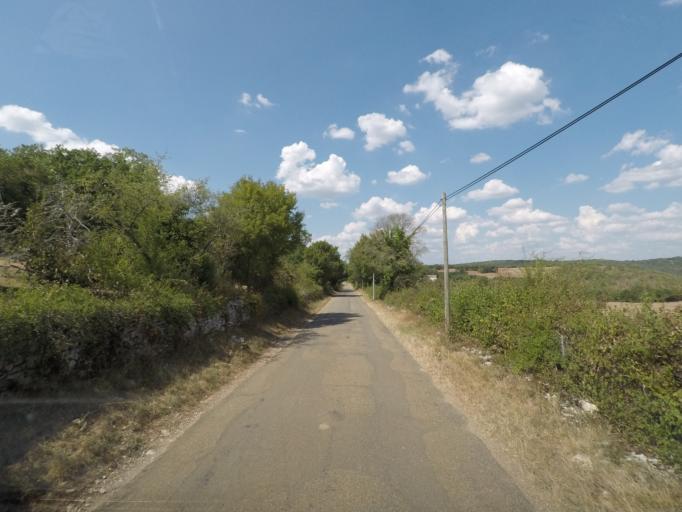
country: FR
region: Midi-Pyrenees
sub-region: Departement du Lot
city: Lalbenque
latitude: 44.5211
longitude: 1.6257
